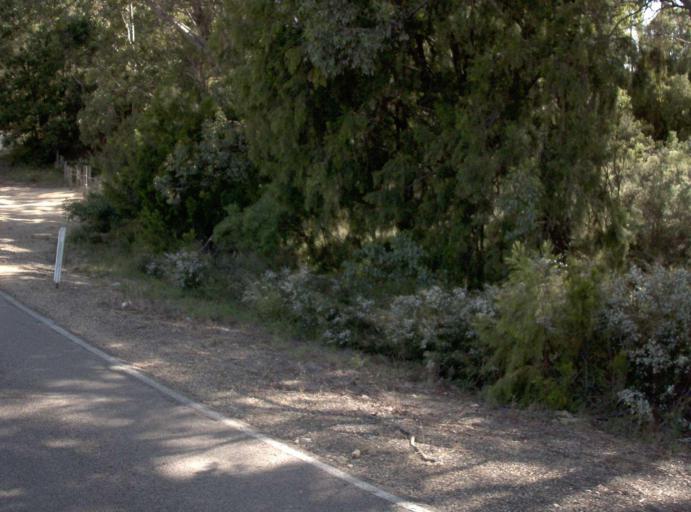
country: AU
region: Victoria
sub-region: East Gippsland
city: Lakes Entrance
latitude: -37.7566
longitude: 147.8145
